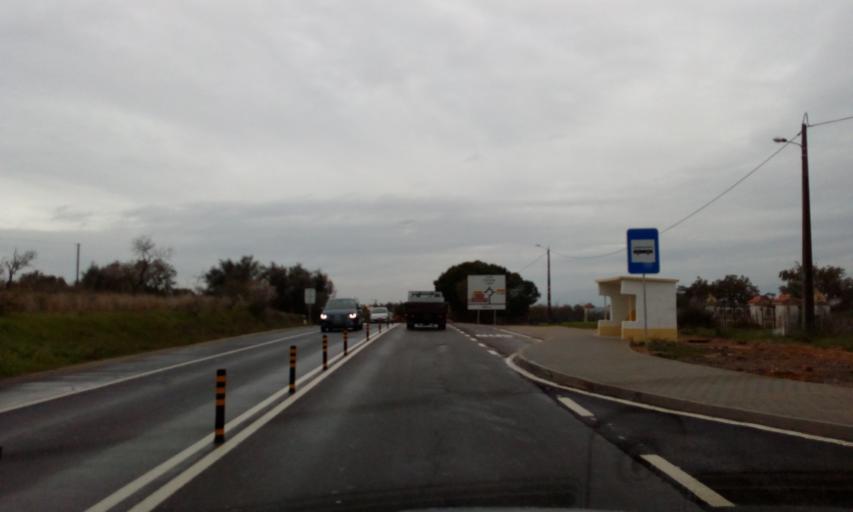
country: PT
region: Faro
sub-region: Lagoa
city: Lagoa
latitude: 37.1277
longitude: -8.4153
